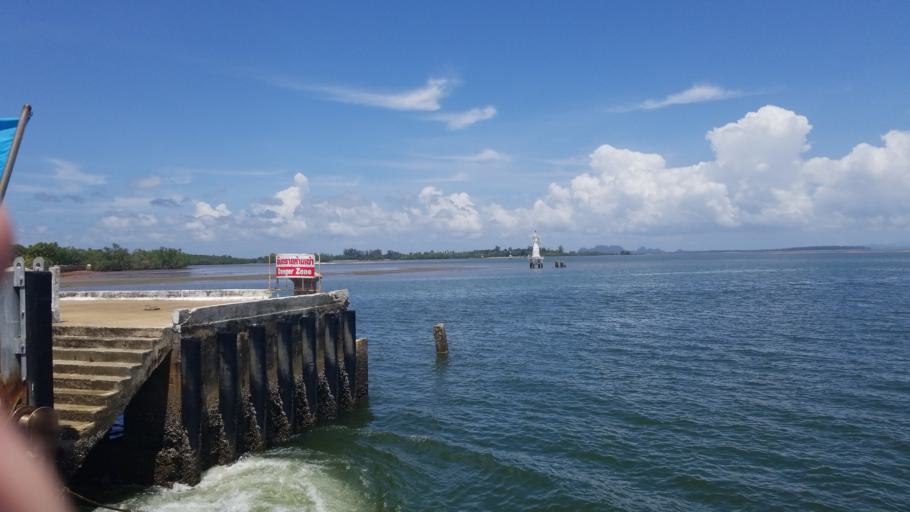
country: TH
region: Krabi
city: Krabi
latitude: 8.0457
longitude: 98.9058
